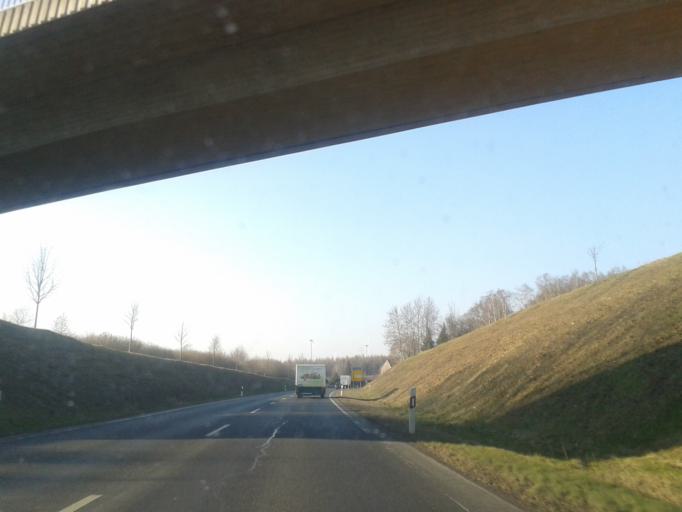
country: DE
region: Saxony
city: Nossen
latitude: 51.0299
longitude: 13.2958
